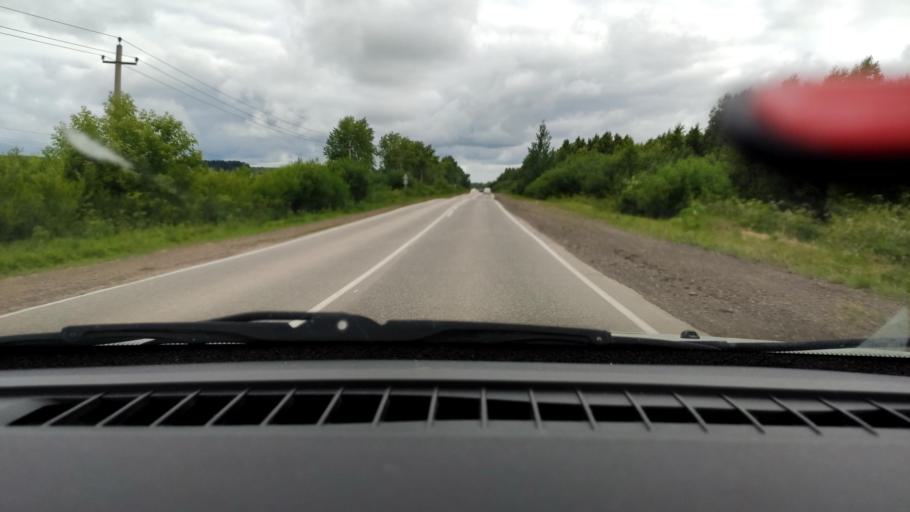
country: RU
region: Perm
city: Chaykovskaya
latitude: 58.0954
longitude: 55.5949
